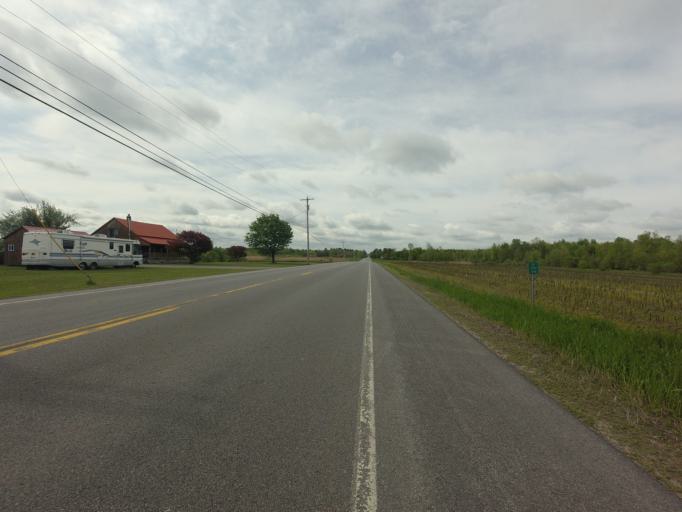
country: CA
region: Ontario
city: Cornwall
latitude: 44.7884
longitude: -74.6751
